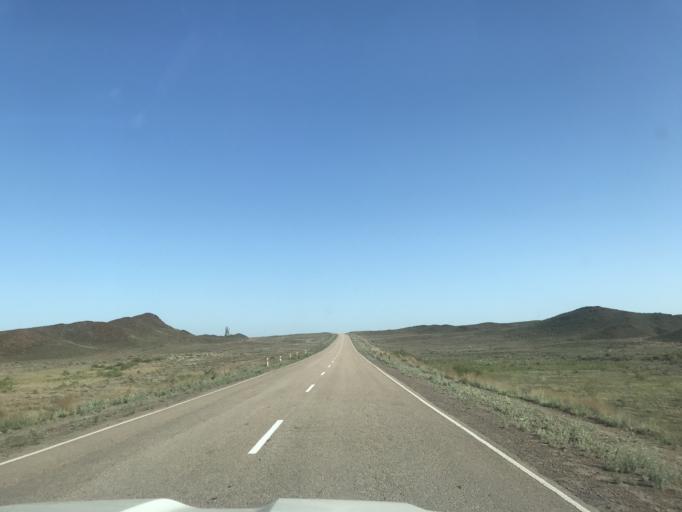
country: KZ
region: Zhambyl
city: Mynaral
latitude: 45.4132
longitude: 73.6284
